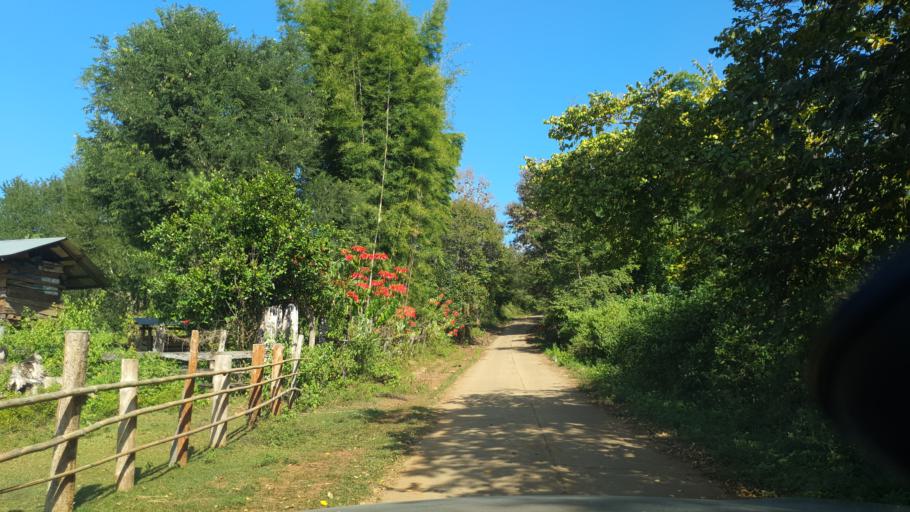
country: TH
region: Mae Hong Son
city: Mae Hi
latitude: 19.2958
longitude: 98.7095
